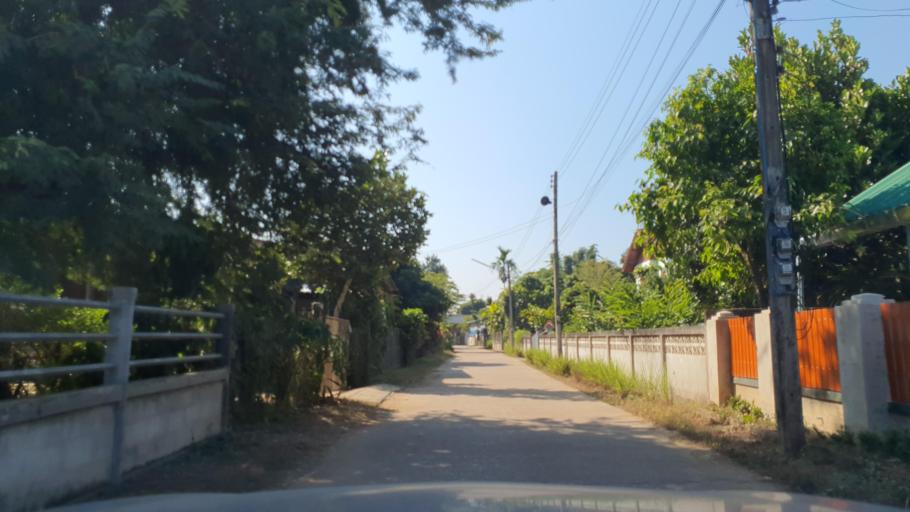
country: TH
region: Lamphun
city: Mae Tha
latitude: 18.5483
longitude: 99.2463
